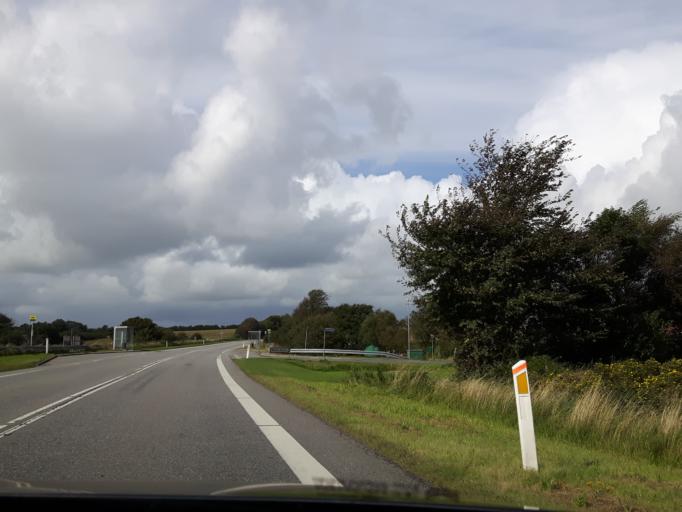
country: DK
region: North Denmark
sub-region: Vesthimmerland Kommune
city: Logstor
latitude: 57.0256
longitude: 9.0061
